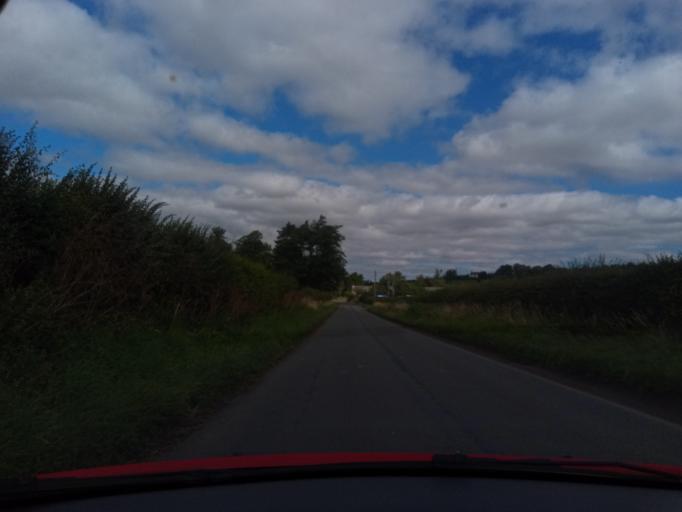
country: GB
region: Scotland
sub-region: The Scottish Borders
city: Kelso
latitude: 55.5334
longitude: -2.3616
